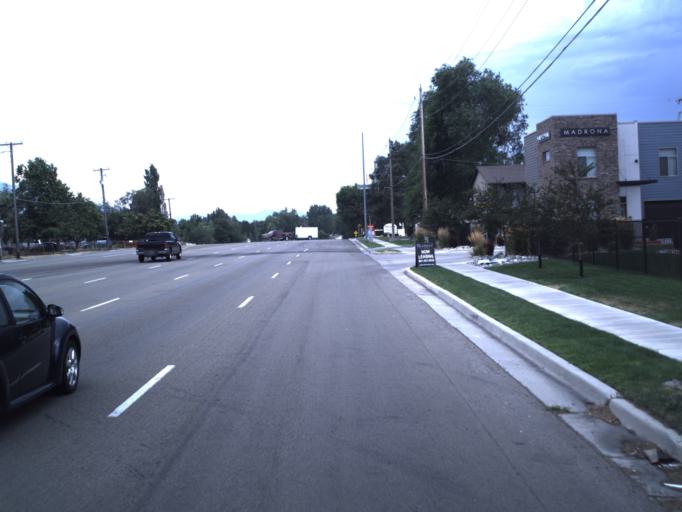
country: US
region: Utah
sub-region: Salt Lake County
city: Millcreek
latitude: 40.6726
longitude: -111.8716
